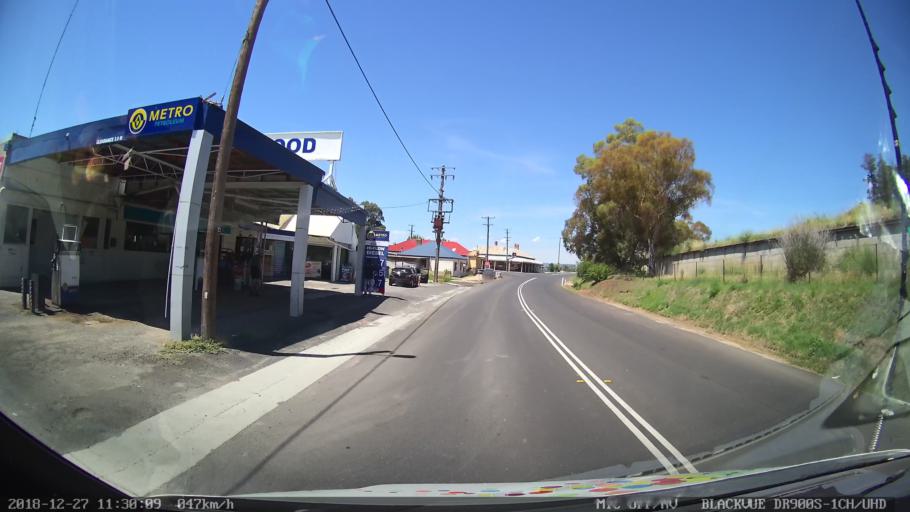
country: AU
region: New South Wales
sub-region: Bathurst Regional
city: Perthville
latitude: -33.4858
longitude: 149.5473
